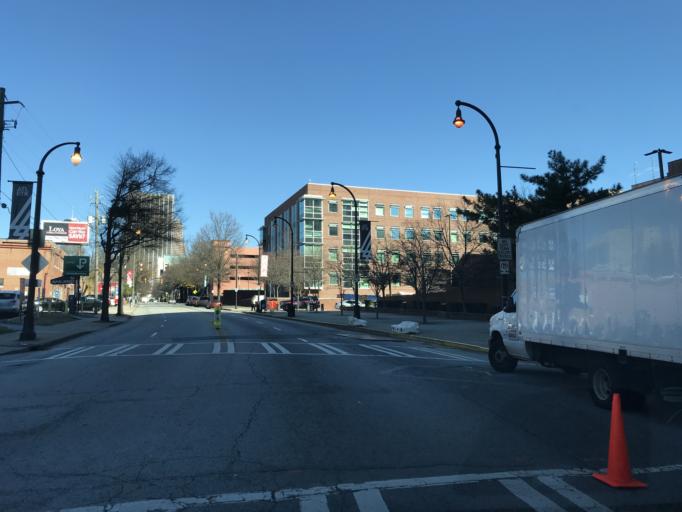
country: US
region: Georgia
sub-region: Fulton County
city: Atlanta
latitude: 33.7476
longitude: -84.3957
